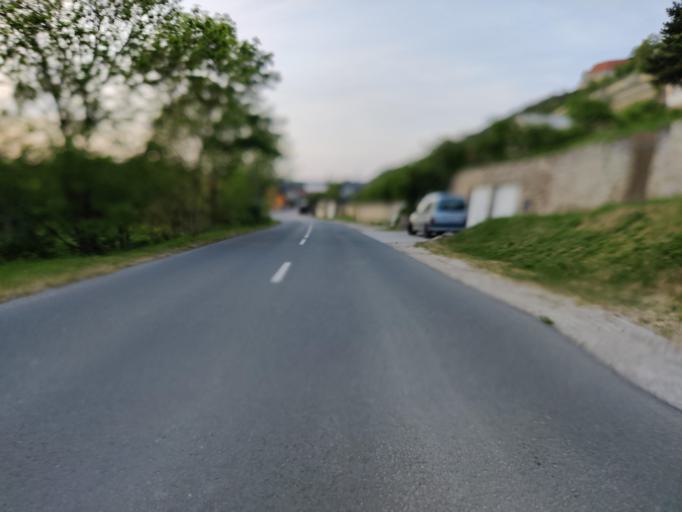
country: DE
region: Saxony-Anhalt
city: Freyburg
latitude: 51.2046
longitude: 11.7744
